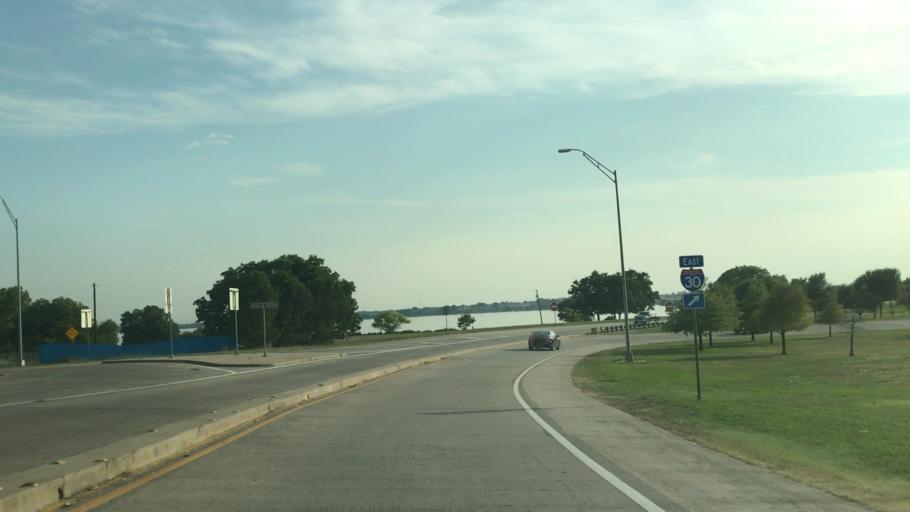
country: US
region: Texas
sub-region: Dallas County
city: Rowlett
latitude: 32.8749
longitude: -96.5194
